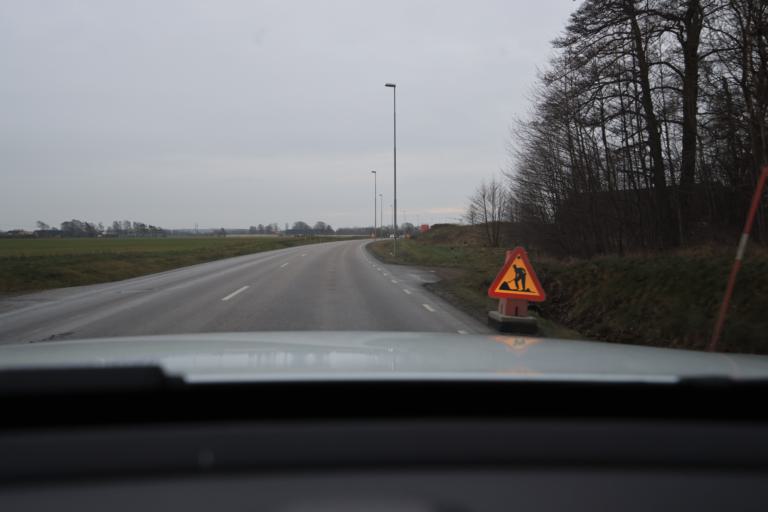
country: SE
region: Halland
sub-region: Varbergs Kommun
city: Traslovslage
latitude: 57.0927
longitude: 12.2937
